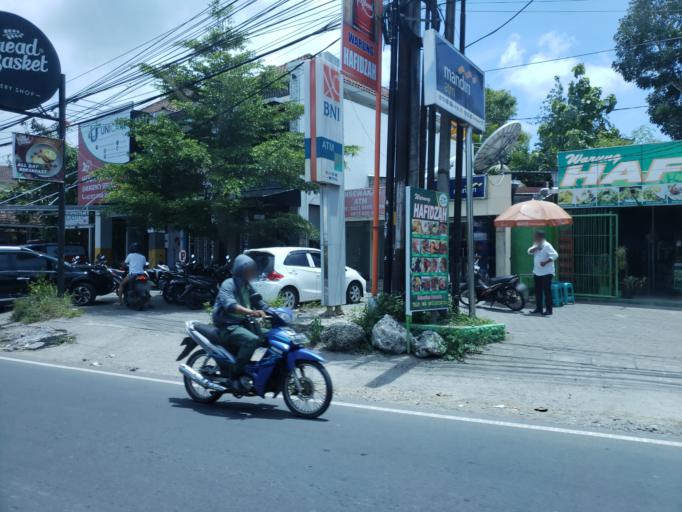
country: ID
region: Bali
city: Kangin
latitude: -8.8218
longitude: 115.1440
